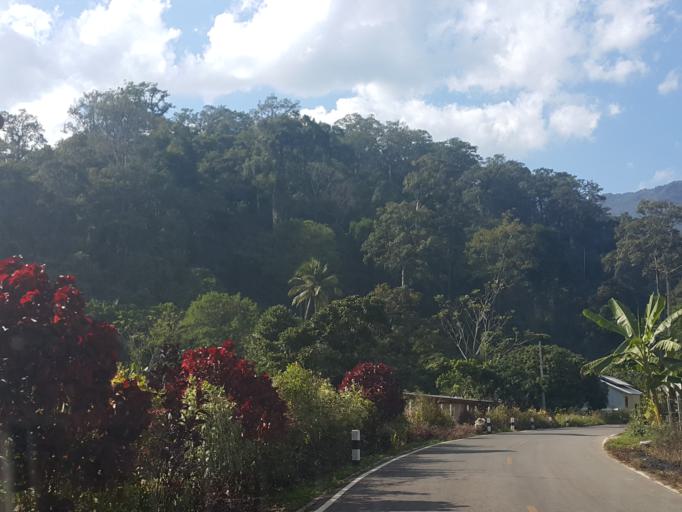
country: TH
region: Chiang Mai
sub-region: Amphoe Chiang Dao
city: Chiang Dao
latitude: 19.4066
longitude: 98.9255
